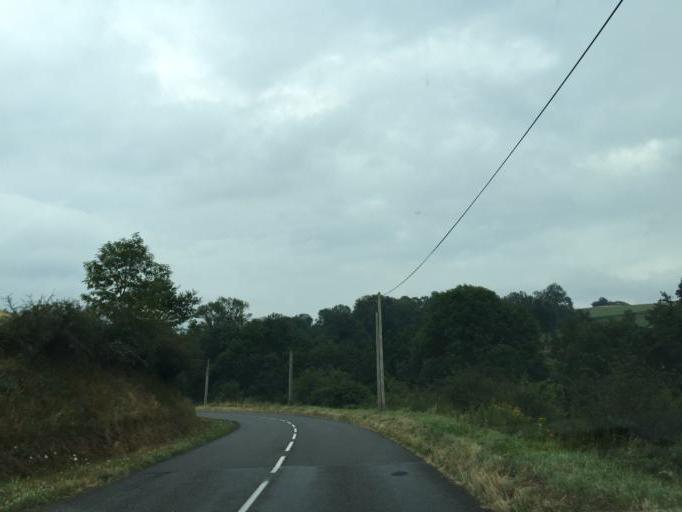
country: FR
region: Rhone-Alpes
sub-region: Departement de la Loire
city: Saint-Christo-en-Jarez
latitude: 45.5295
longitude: 4.4709
